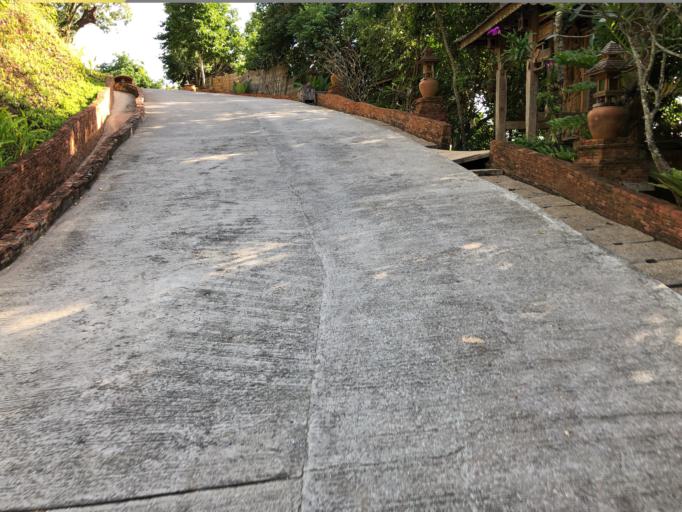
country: TH
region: Phangnga
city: Ban Phru Nai
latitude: 7.9849
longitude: 98.5669
